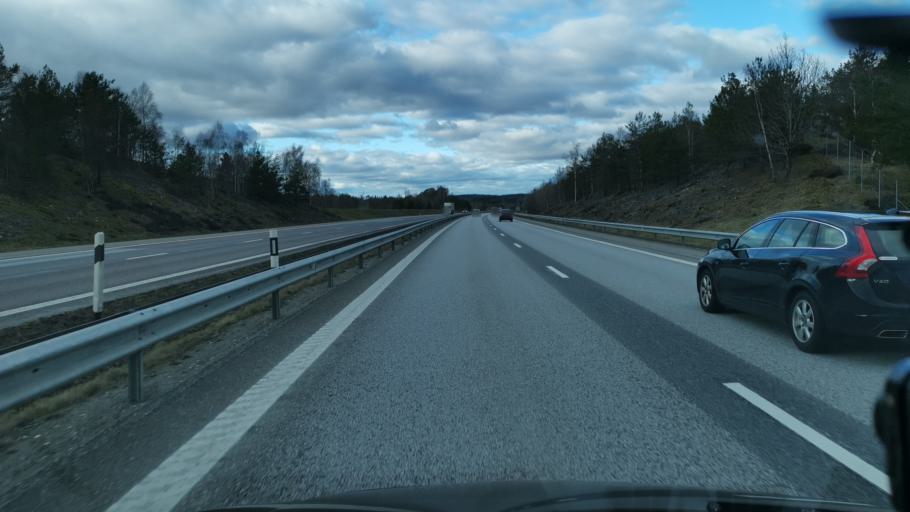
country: SE
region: Vaestra Goetaland
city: Svanesund
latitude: 58.0906
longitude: 11.8825
